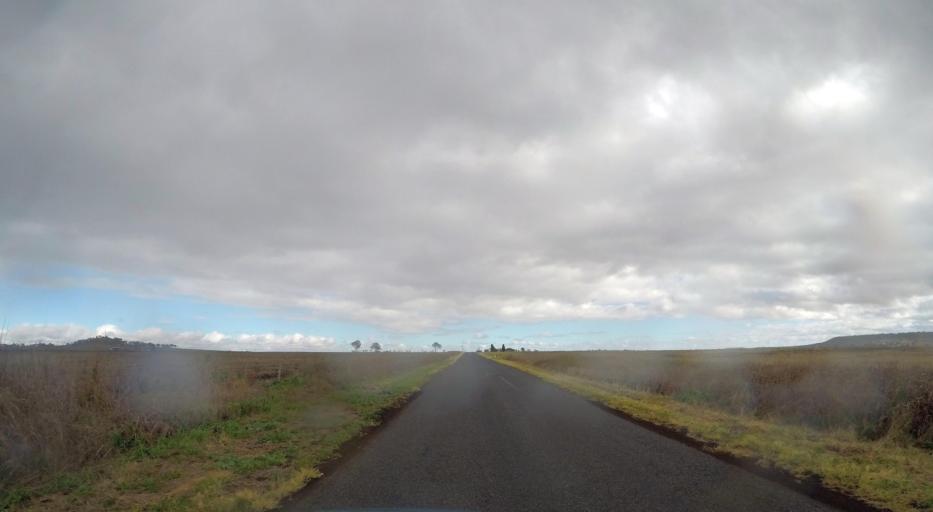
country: AU
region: Queensland
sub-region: Southern Downs
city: Warwick
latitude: -28.0494
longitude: 152.0387
